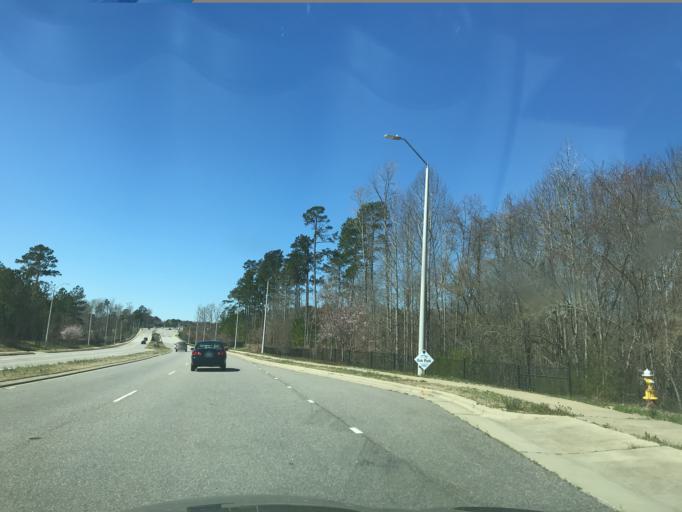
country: US
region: North Carolina
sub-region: Wake County
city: Garner
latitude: 35.6877
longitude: -78.5935
